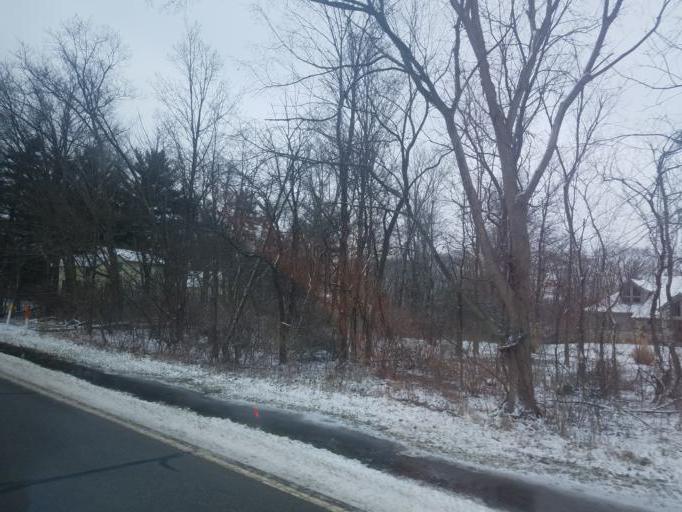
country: US
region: Ohio
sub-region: Franklin County
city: New Albany
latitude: 40.0932
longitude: -82.7816
